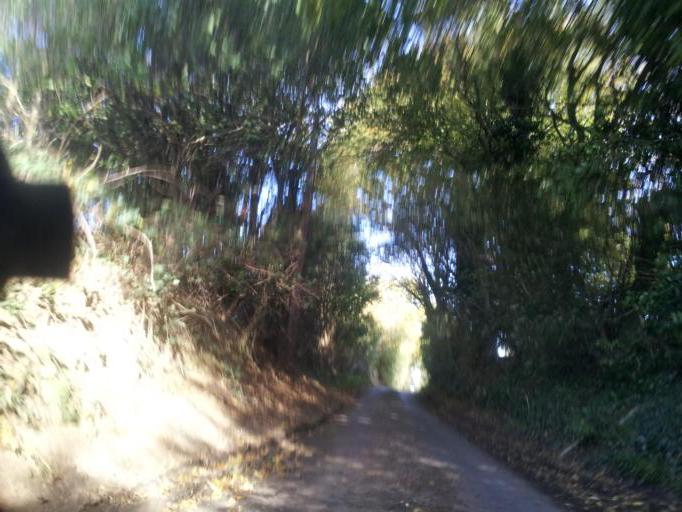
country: GB
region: England
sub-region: Kent
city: Newington
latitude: 51.3690
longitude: 0.6538
